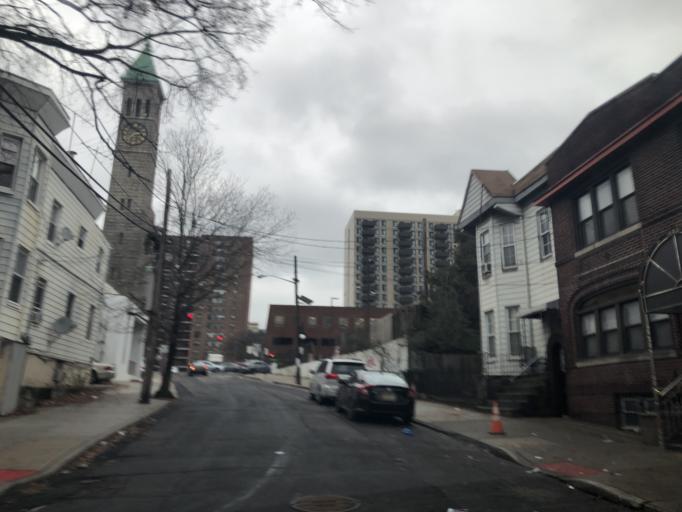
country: US
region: New Jersey
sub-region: Hudson County
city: Jersey City
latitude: 40.7362
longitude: -74.0641
